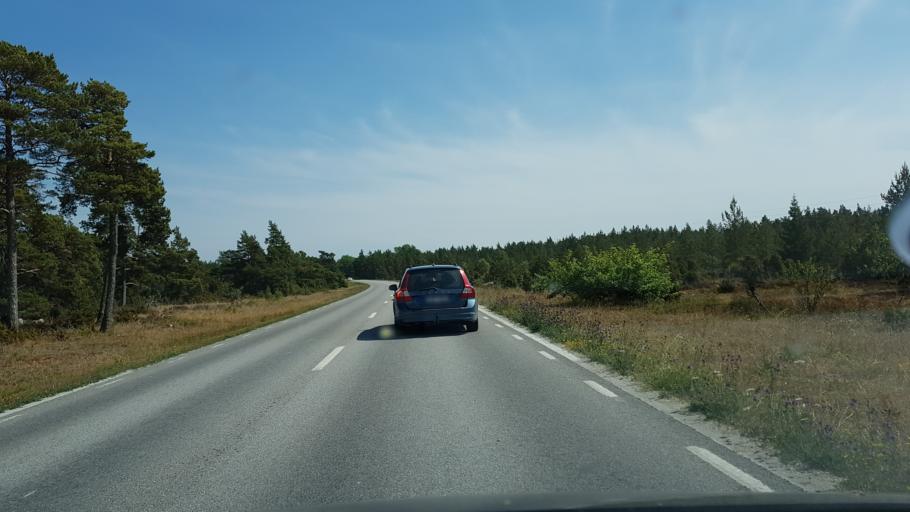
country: SE
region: Gotland
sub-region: Gotland
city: Visby
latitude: 57.6341
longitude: 18.4072
